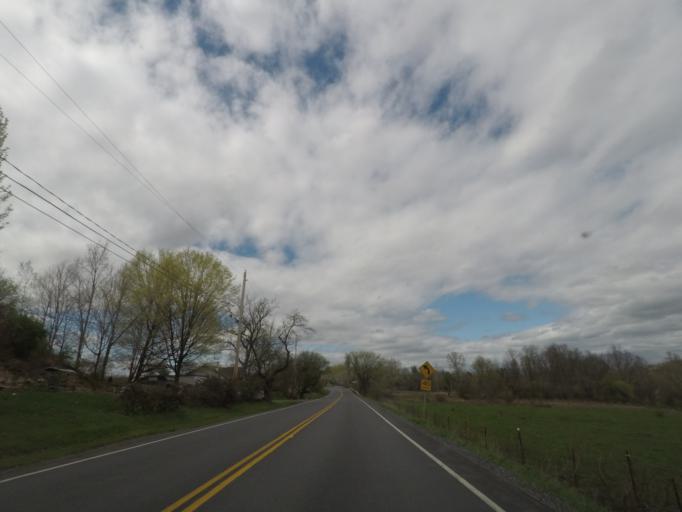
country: US
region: New York
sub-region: Columbia County
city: Valatie
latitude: 42.3923
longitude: -73.6436
